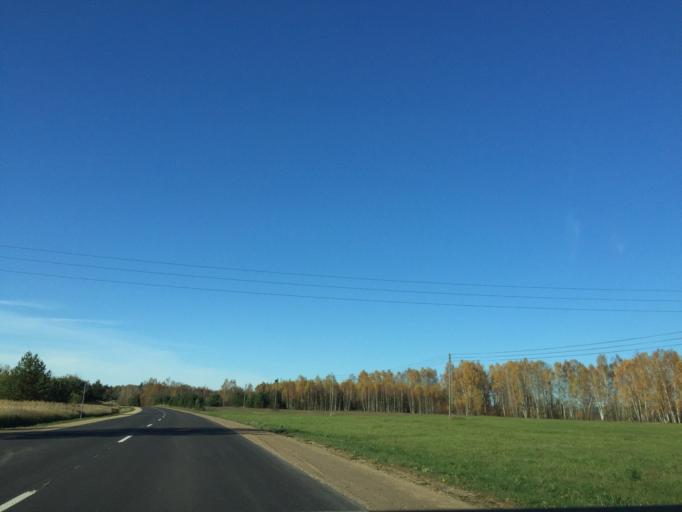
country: LV
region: Aizkraukles Rajons
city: Aizkraukle
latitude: 56.5896
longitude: 25.1882
